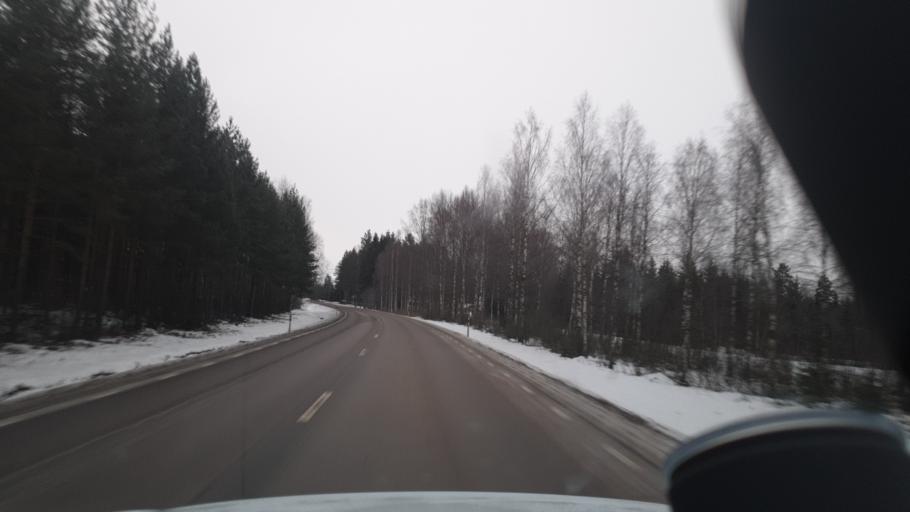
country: SE
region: Vaermland
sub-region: Eda Kommun
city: Charlottenberg
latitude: 59.8437
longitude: 12.3128
